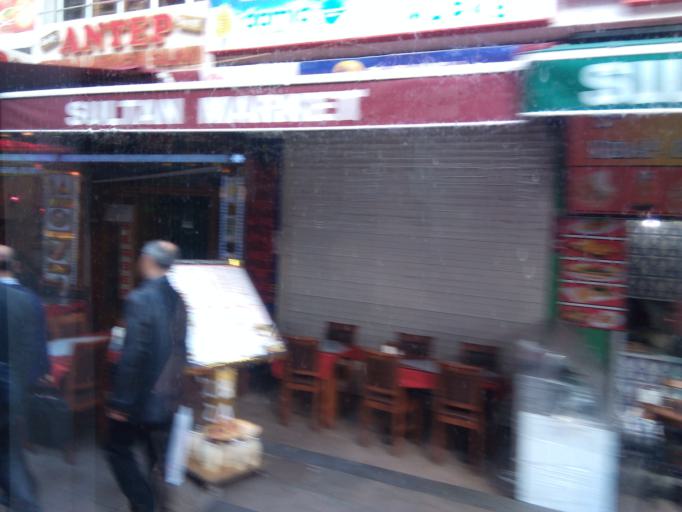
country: TR
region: Istanbul
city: Eminoenue
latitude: 41.0139
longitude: 28.9770
